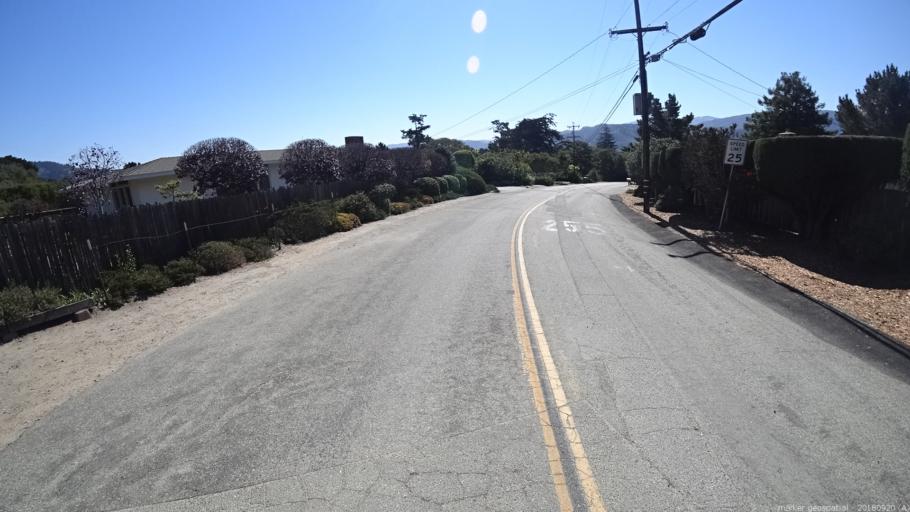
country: US
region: California
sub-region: Monterey County
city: Carmel-by-the-Sea
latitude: 36.5527
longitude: -121.9101
